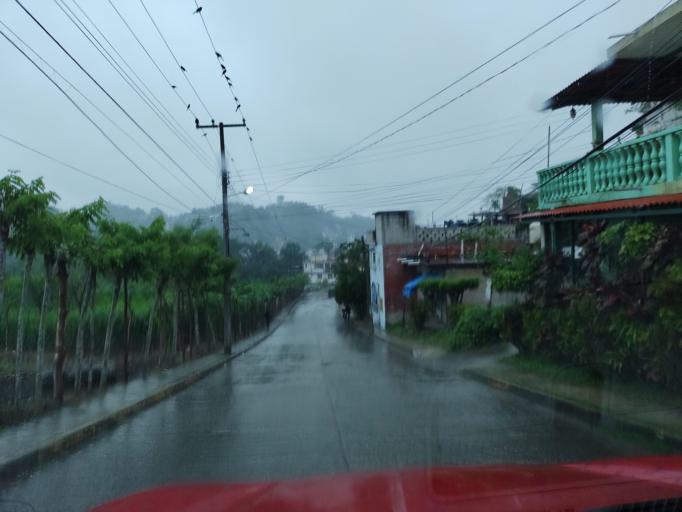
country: MX
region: Veracruz
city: Papantla de Olarte
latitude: 20.4392
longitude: -97.3366
